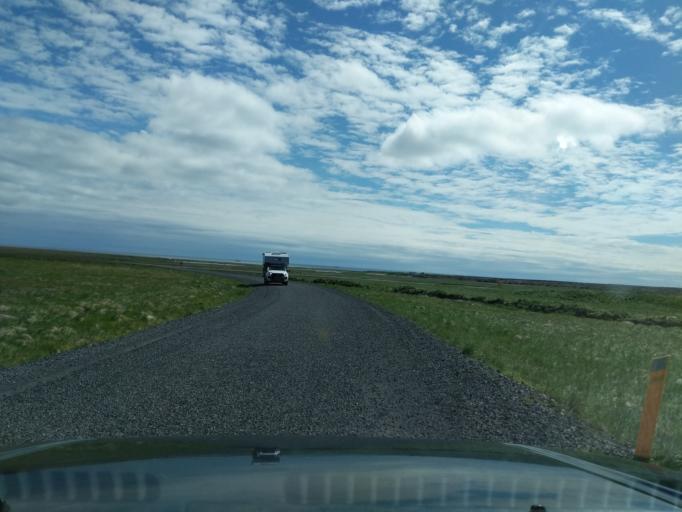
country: IS
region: West
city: Olafsvik
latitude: 64.8424
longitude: -23.4001
